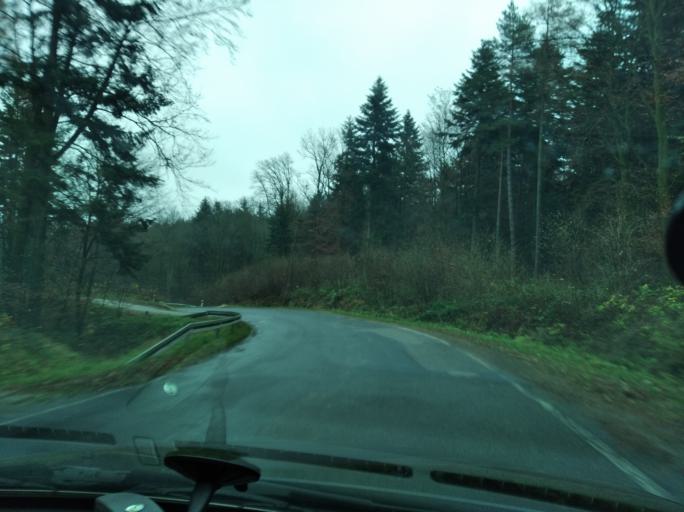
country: PL
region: Subcarpathian Voivodeship
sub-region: Powiat przeworski
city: Jawornik Polski
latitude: 49.8844
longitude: 22.2552
